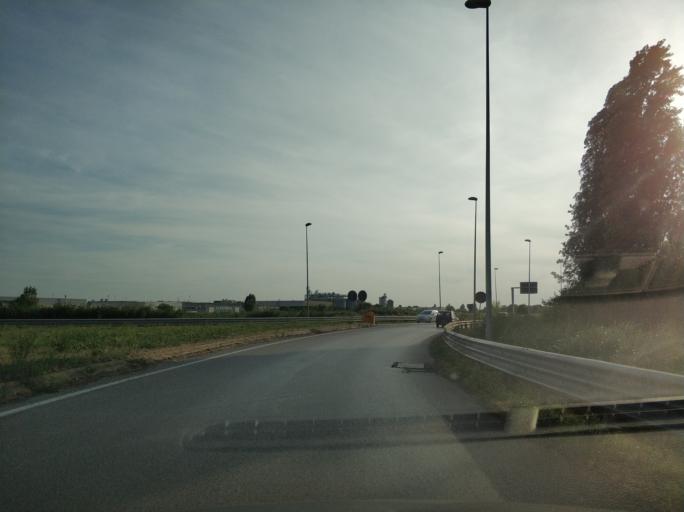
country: IT
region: Veneto
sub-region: Provincia di Padova
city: Arre
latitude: 45.2125
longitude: 11.9021
